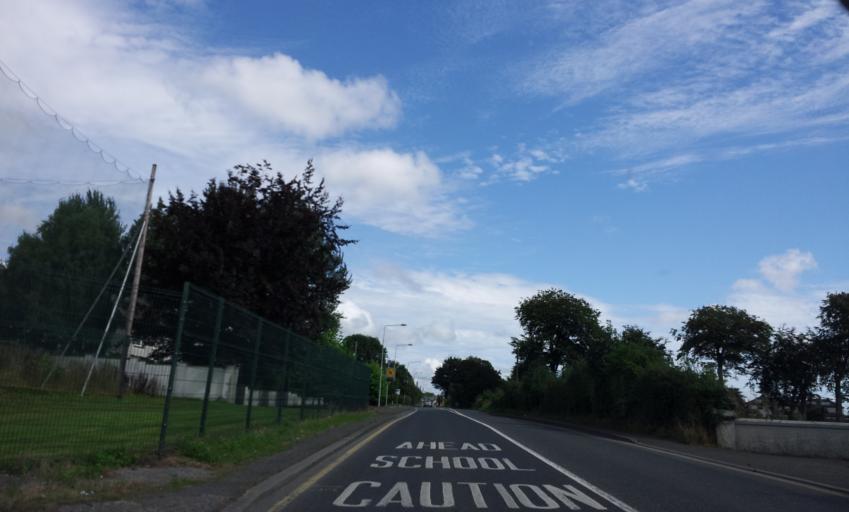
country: IE
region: Leinster
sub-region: Laois
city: Mountrath
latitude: 52.9941
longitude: -7.4826
